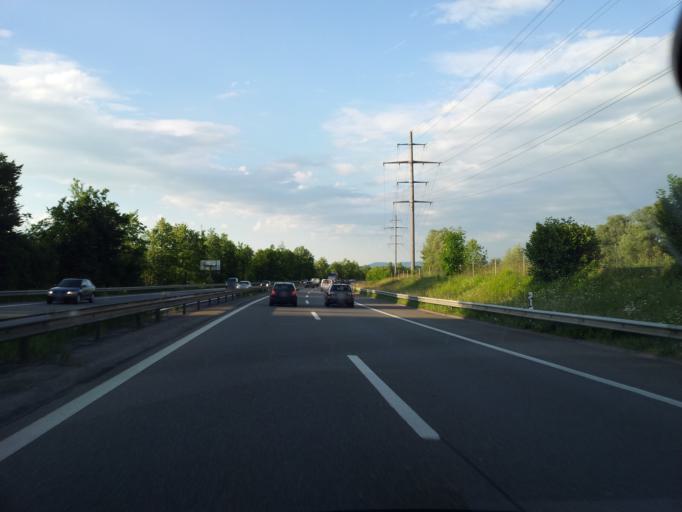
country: CH
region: Lucerne
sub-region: Lucerne-Land District
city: Root
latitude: 47.1339
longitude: 8.3990
